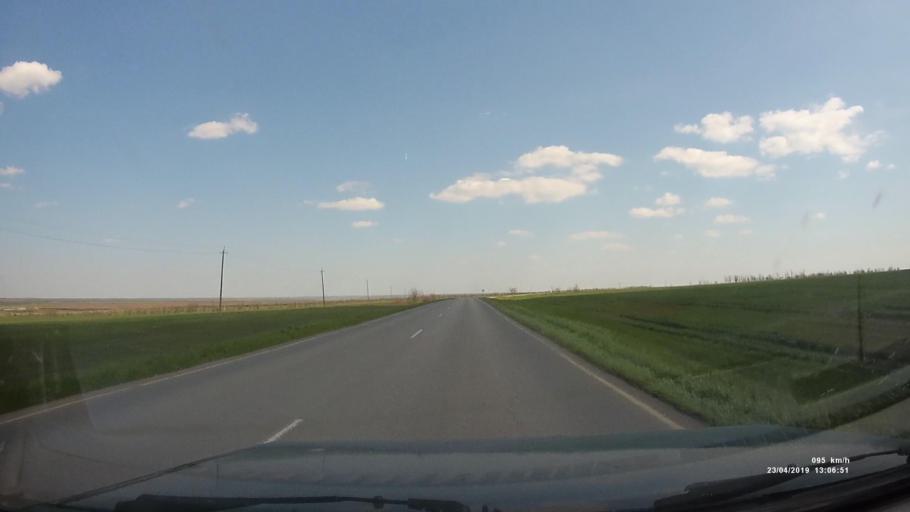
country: RU
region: Kalmykiya
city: Yashalta
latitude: 46.5918
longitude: 42.7494
